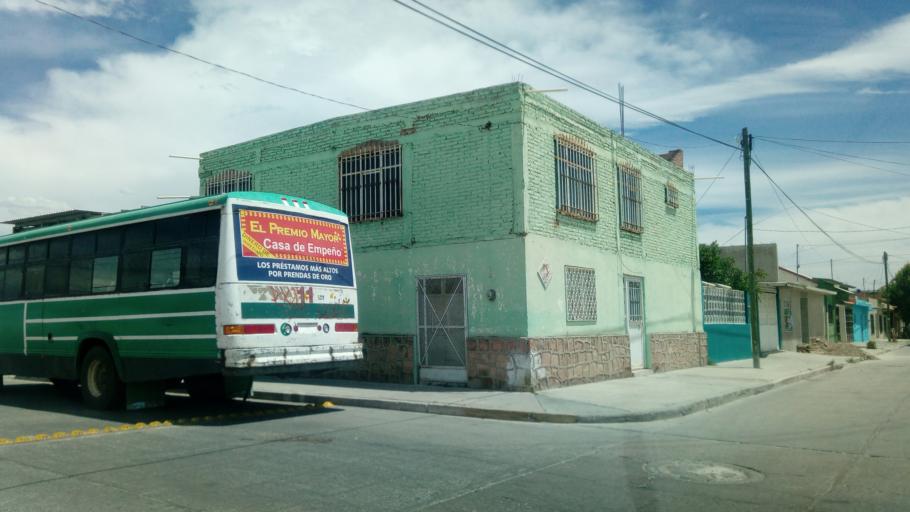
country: MX
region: Durango
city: Victoria de Durango
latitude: 23.9943
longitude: -104.6765
